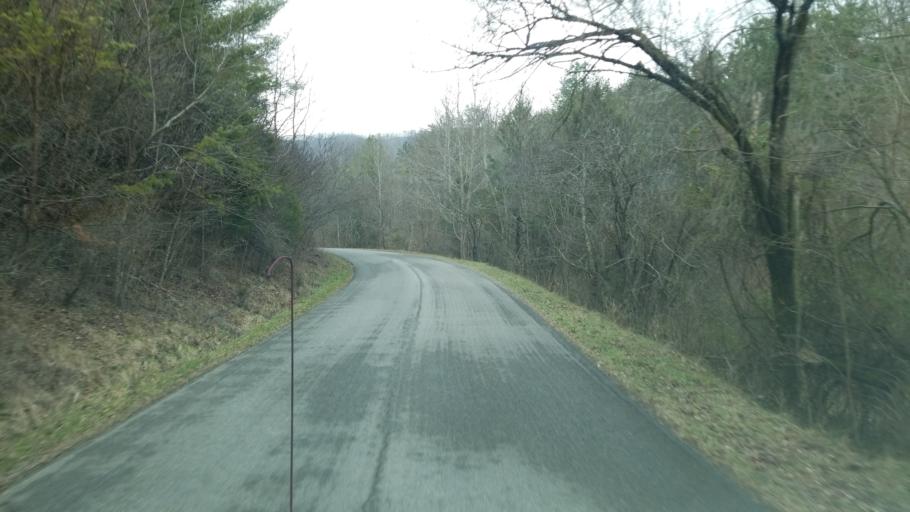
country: US
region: Virginia
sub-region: Giles County
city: Pearisburg
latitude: 37.2266
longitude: -80.6998
